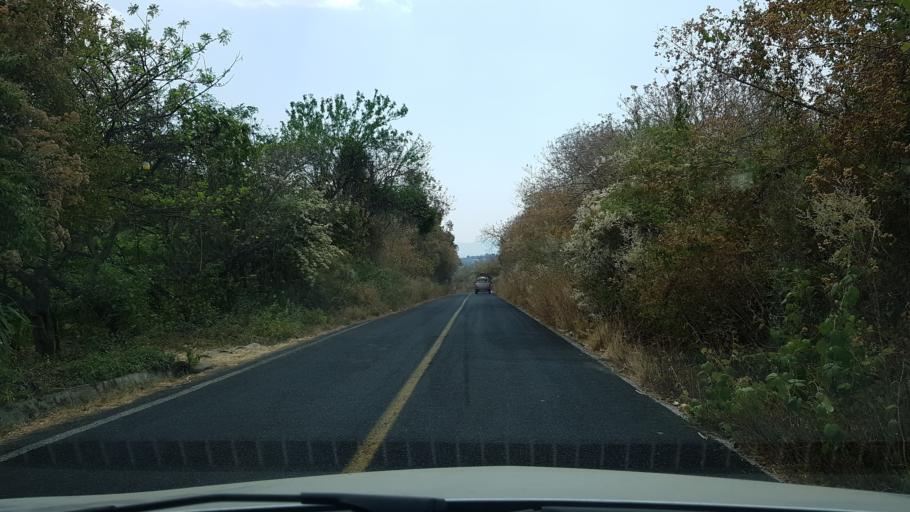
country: MX
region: Morelos
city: Tlacotepec
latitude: 18.8368
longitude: -98.7333
